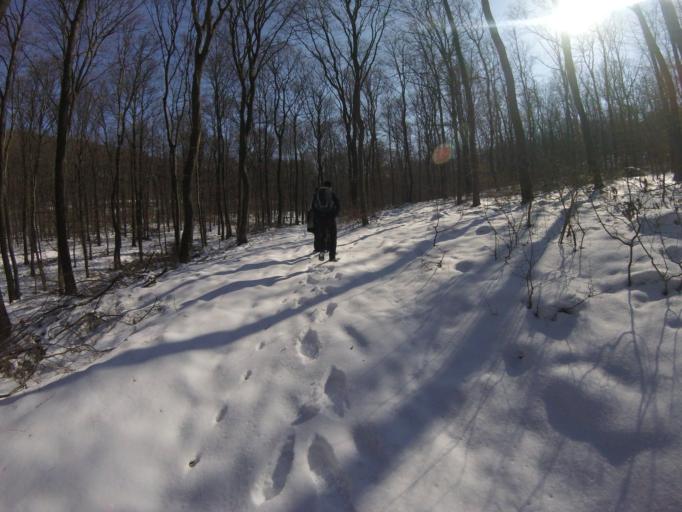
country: HU
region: Komarom-Esztergom
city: Piliscsev
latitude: 47.6873
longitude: 18.8481
